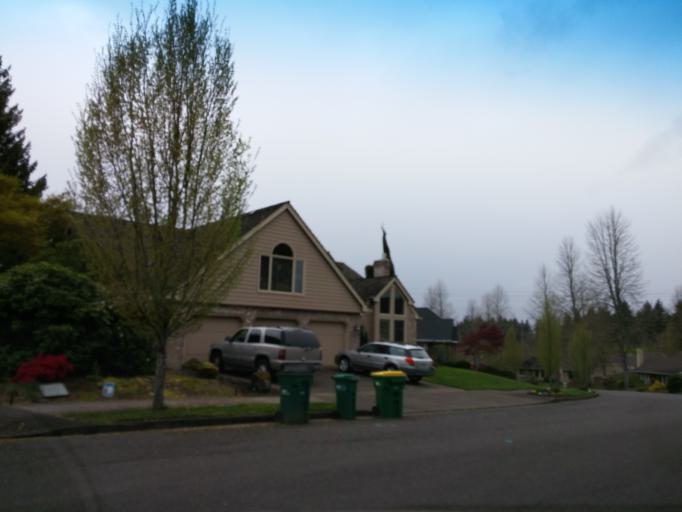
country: US
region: Oregon
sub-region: Washington County
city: Oak Hills
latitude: 45.5256
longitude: -122.8439
